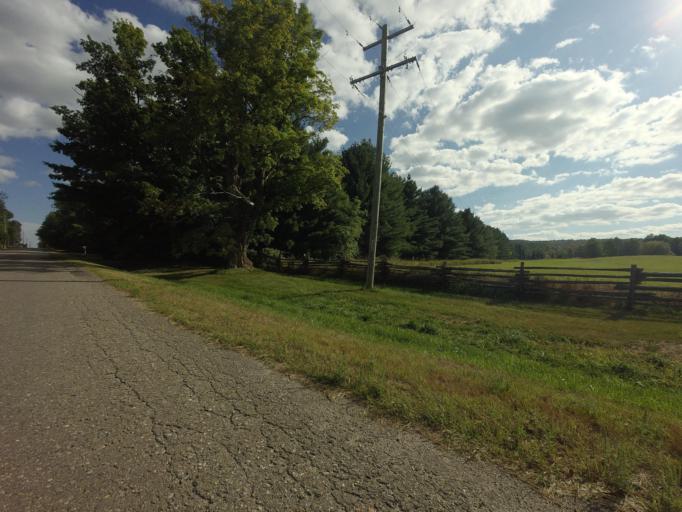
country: CA
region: Ontario
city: Orangeville
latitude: 43.8041
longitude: -79.9439
